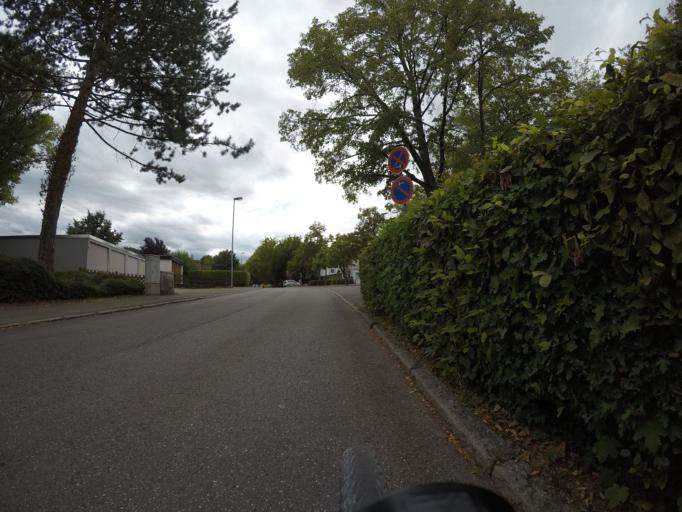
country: DE
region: Baden-Wuerttemberg
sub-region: Tuebingen Region
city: Reutlingen
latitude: 48.4779
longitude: 9.1953
